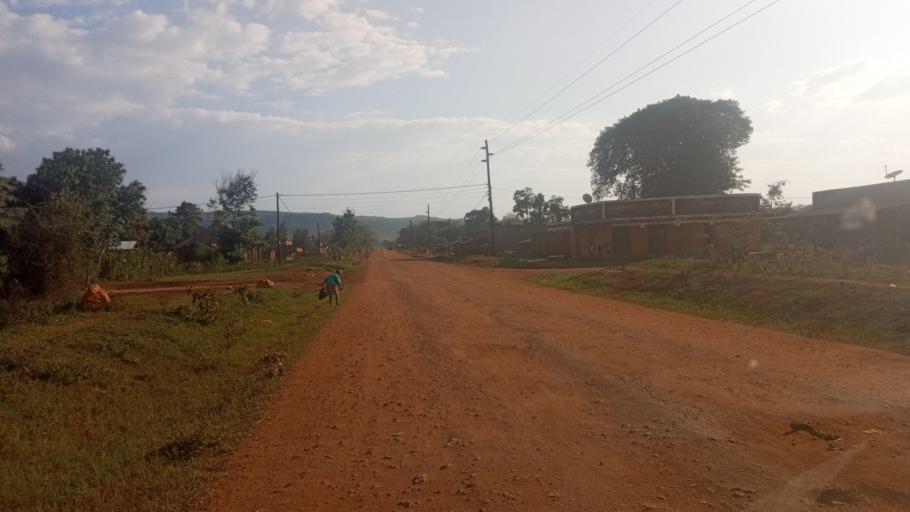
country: UG
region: Eastern Region
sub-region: Kapchorwa District
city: Kapchorwa
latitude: 1.4189
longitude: 34.3513
